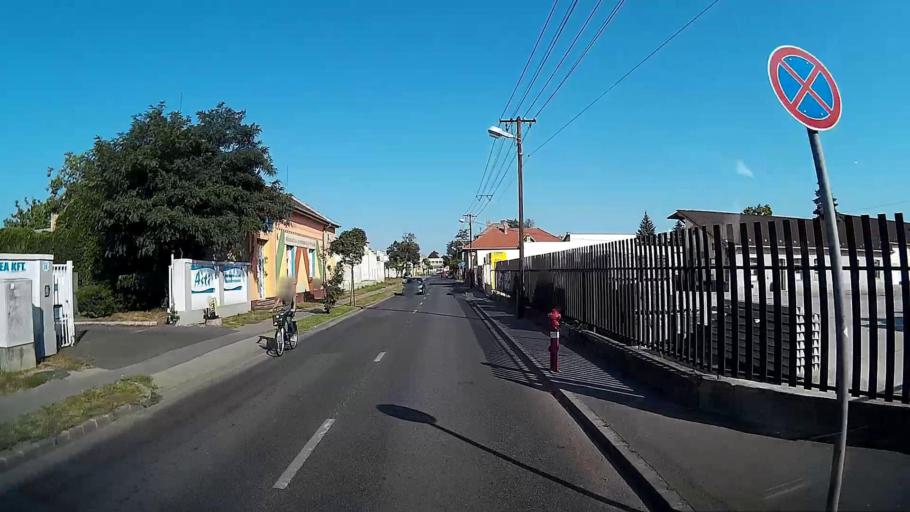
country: HU
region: Budapest
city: Budapest XX. keruelet
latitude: 47.4278
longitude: 19.1074
